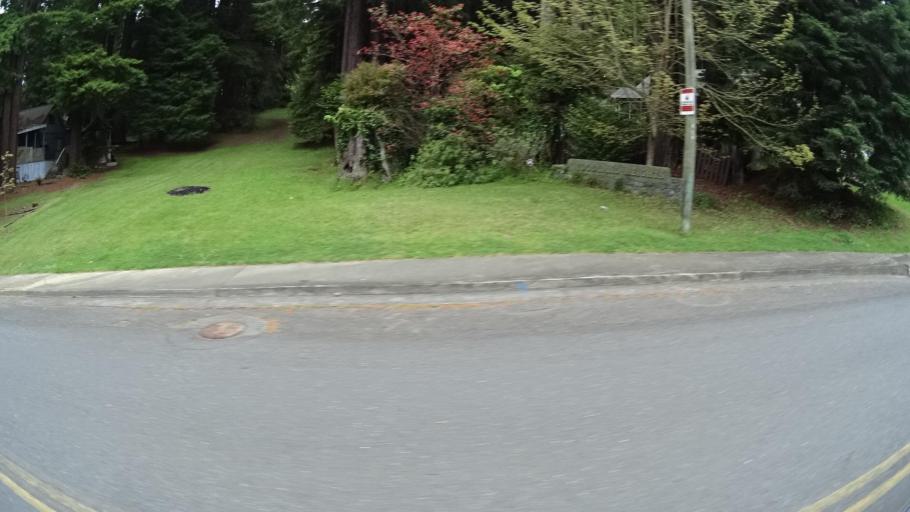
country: US
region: California
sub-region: Humboldt County
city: Arcata
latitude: 40.8878
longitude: -124.0774
